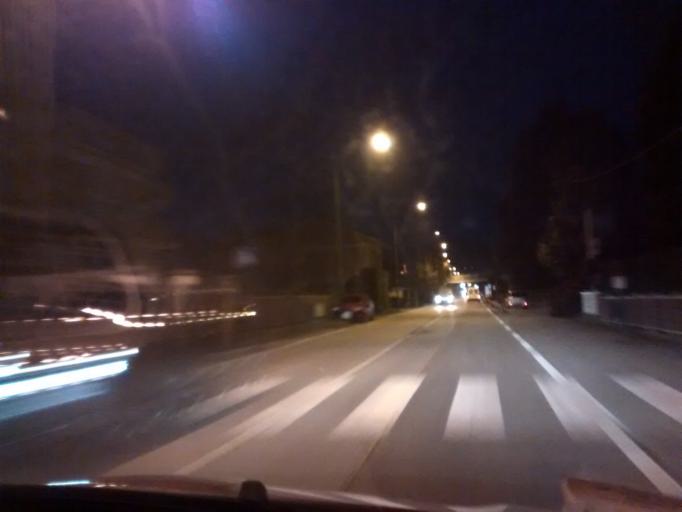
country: IT
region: Piedmont
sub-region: Provincia di Torino
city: Pinerolo
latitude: 44.8696
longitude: 7.3348
